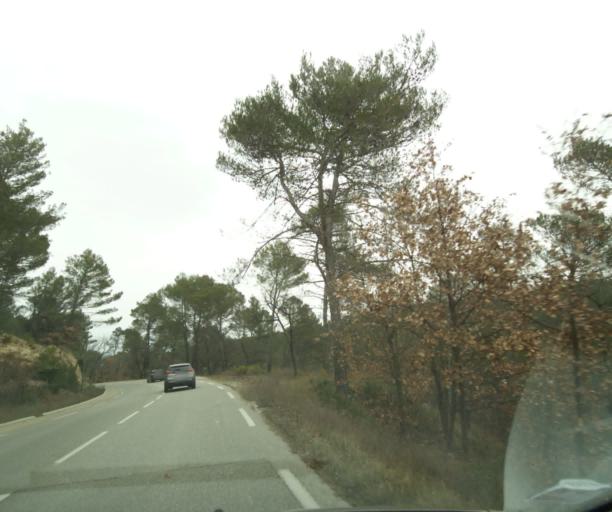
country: FR
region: Provence-Alpes-Cote d'Azur
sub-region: Departement des Bouches-du-Rhone
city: Peynier
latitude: 43.4391
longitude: 5.6298
